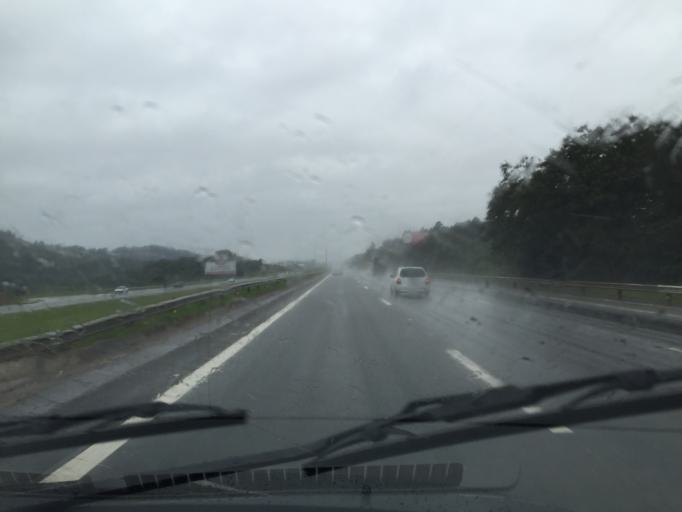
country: BR
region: Sao Paulo
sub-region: Sao Roque
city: Sao Roque
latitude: -23.4200
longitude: -47.1969
